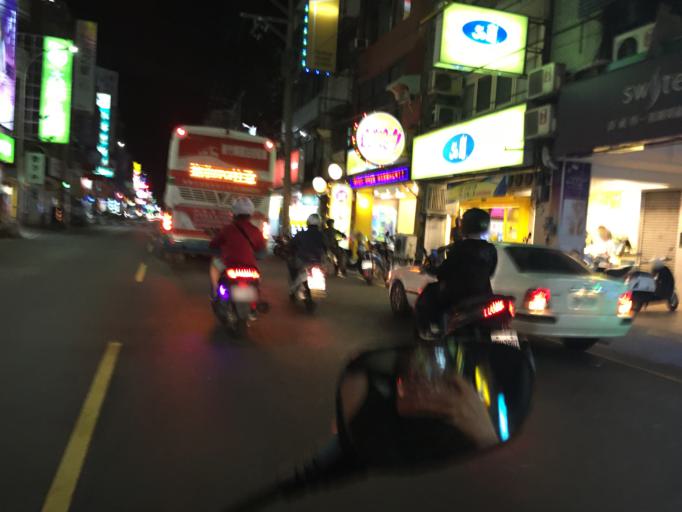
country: TW
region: Taiwan
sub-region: Hsinchu
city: Hsinchu
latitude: 24.7977
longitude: 120.9699
